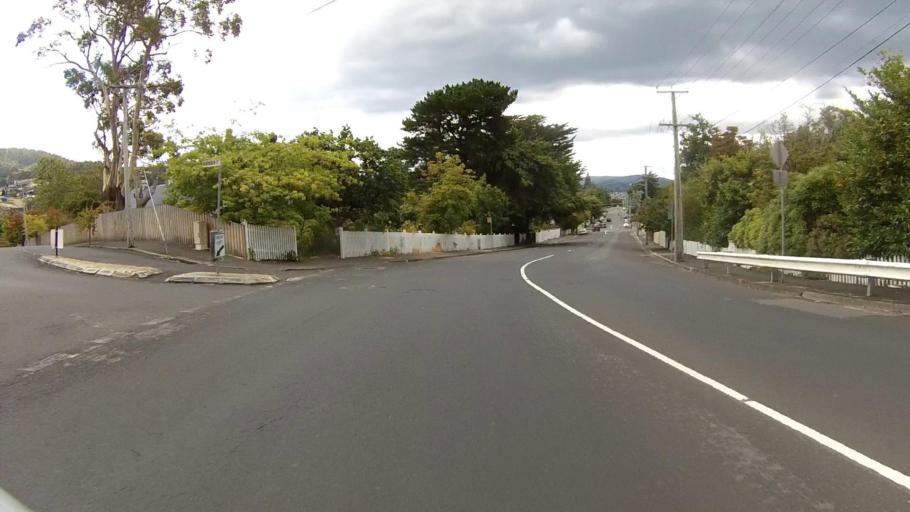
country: AU
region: Tasmania
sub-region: Hobart
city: Dynnyrne
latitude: -42.8990
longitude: 147.3125
